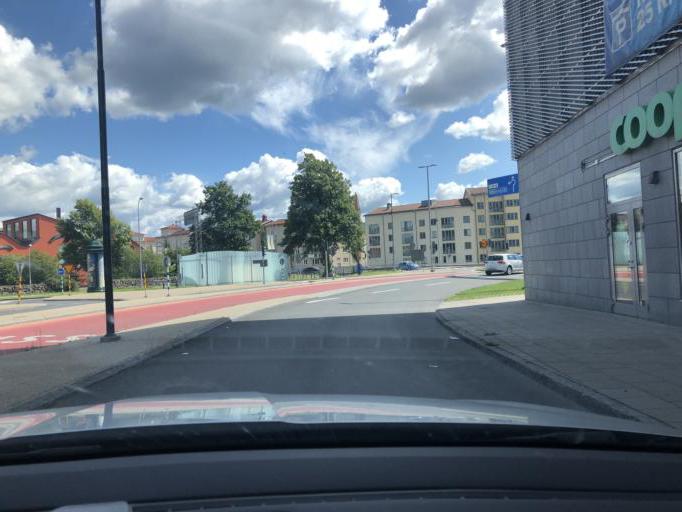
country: SE
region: Joenkoeping
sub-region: Jonkopings Kommun
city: Jonkoping
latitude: 57.7806
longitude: 14.1736
